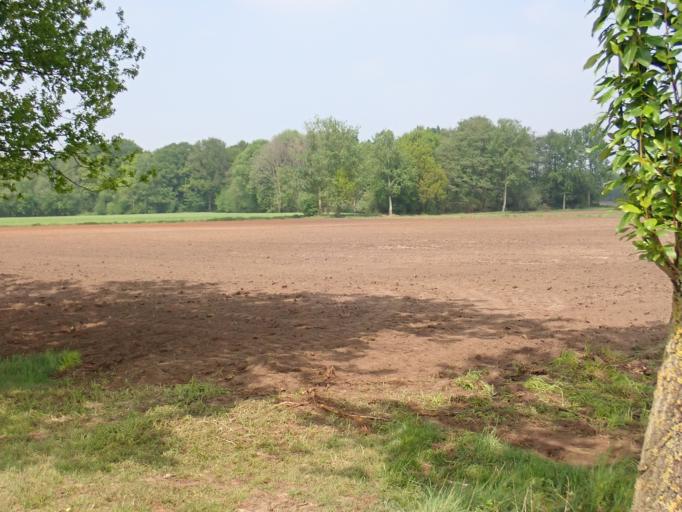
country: BE
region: Flanders
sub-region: Provincie Antwerpen
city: Herentals
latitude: 51.2089
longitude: 4.8393
